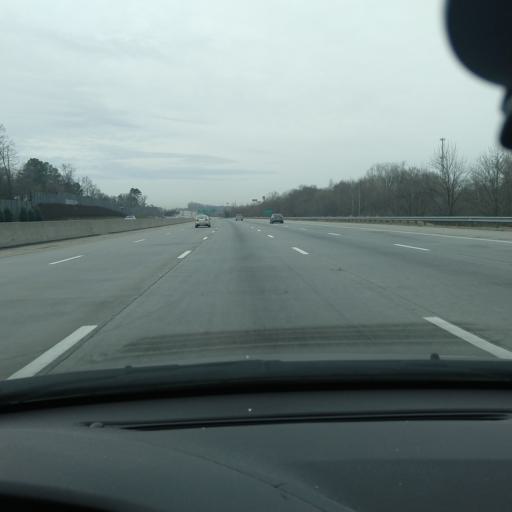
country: US
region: North Carolina
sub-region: Rowan County
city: Salisbury
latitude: 35.6628
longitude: -80.4506
